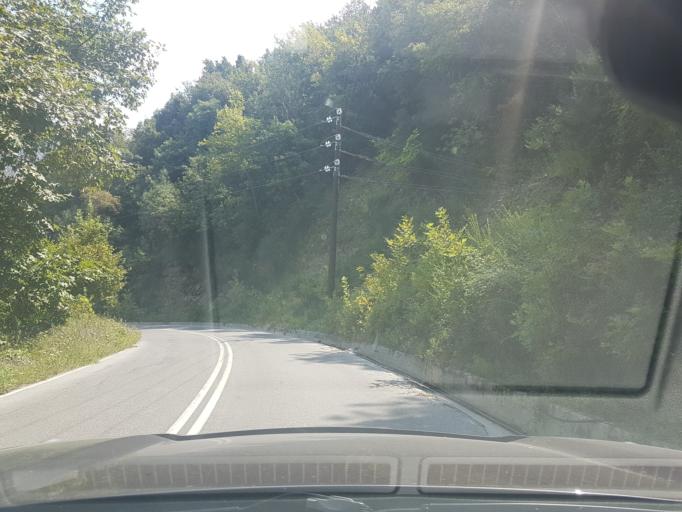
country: GR
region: Central Greece
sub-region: Nomos Evvoias
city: Kymi
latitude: 38.6384
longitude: 23.9402
